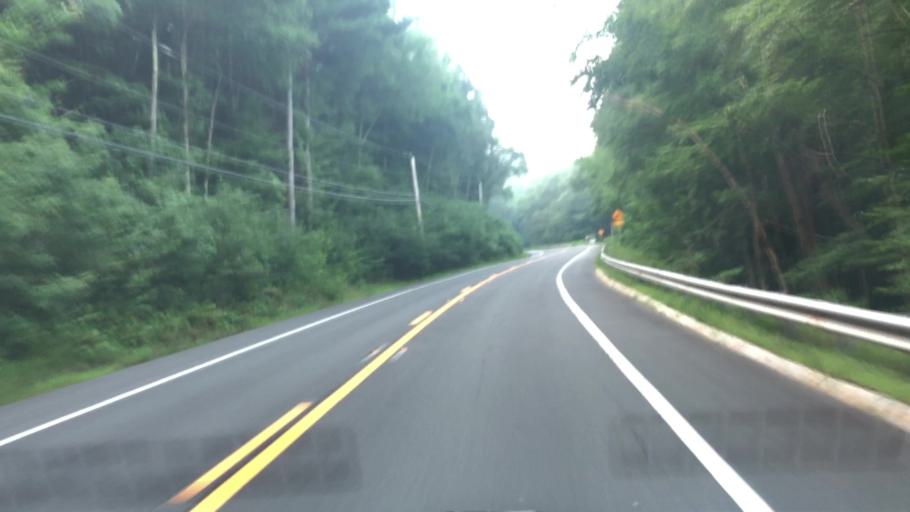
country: US
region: Massachusetts
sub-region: Franklin County
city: Ashfield
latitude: 42.5472
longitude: -72.8013
